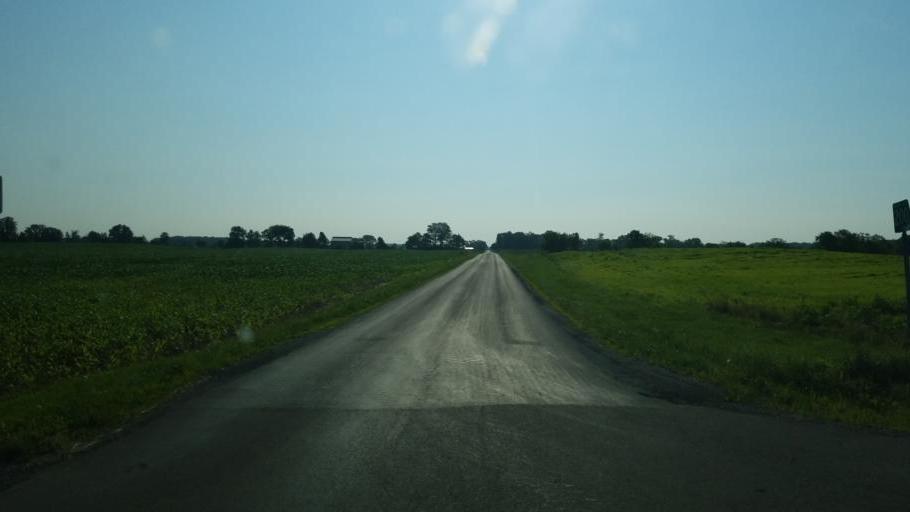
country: US
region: Ohio
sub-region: Hardin County
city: Kenton
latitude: 40.5627
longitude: -83.5443
